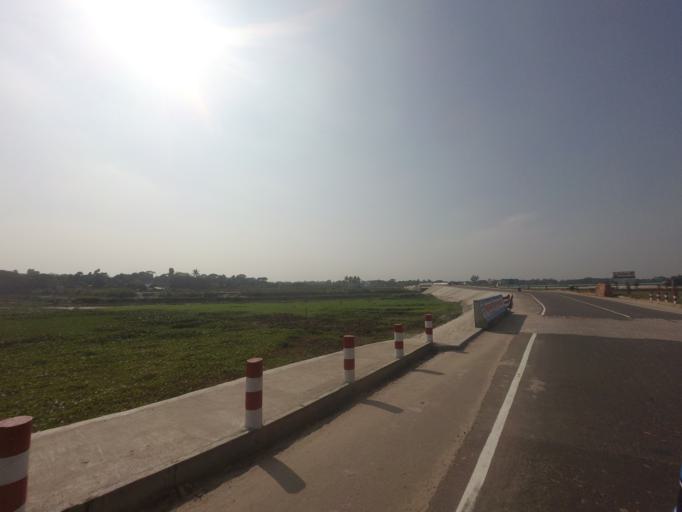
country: BD
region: Dhaka
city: Azimpur
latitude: 23.7354
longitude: 90.3288
